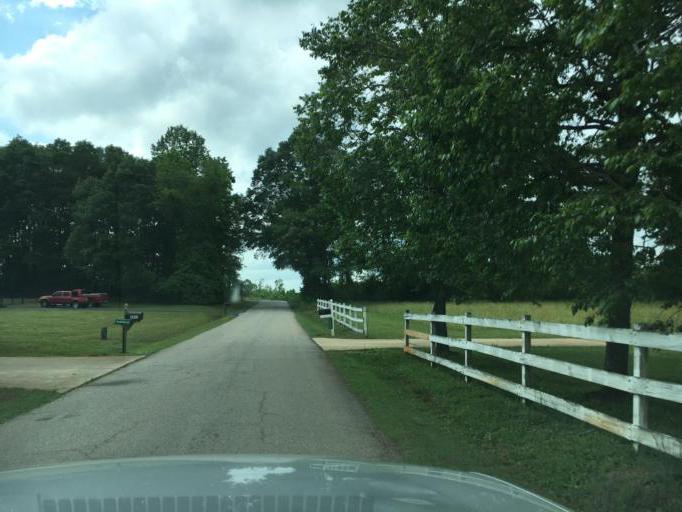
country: US
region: South Carolina
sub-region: Spartanburg County
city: Fairforest
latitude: 34.9195
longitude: -82.0459
